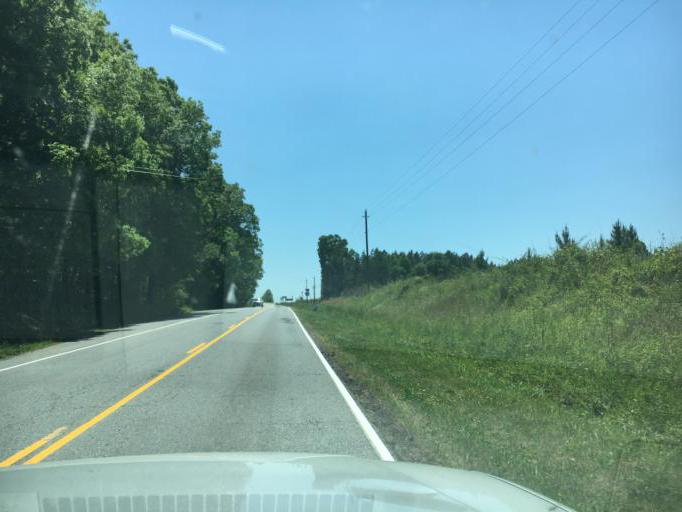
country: US
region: South Carolina
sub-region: Cherokee County
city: East Gaffney
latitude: 35.1141
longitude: -81.6011
